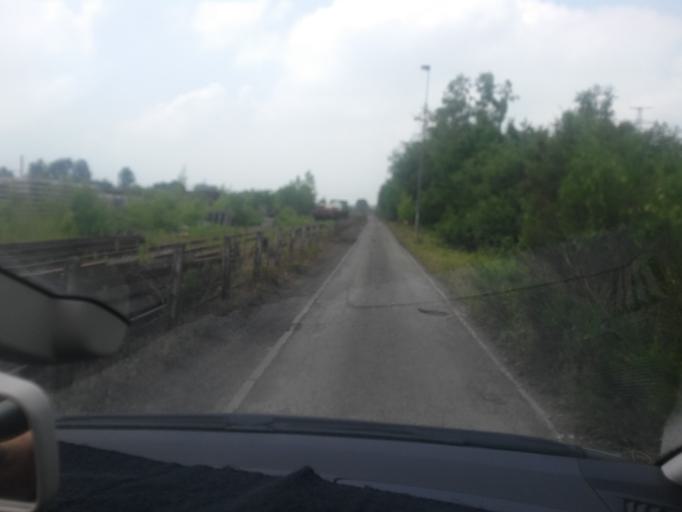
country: BE
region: Wallonia
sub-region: Province du Luxembourg
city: Arlon
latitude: 49.6917
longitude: 5.7608
